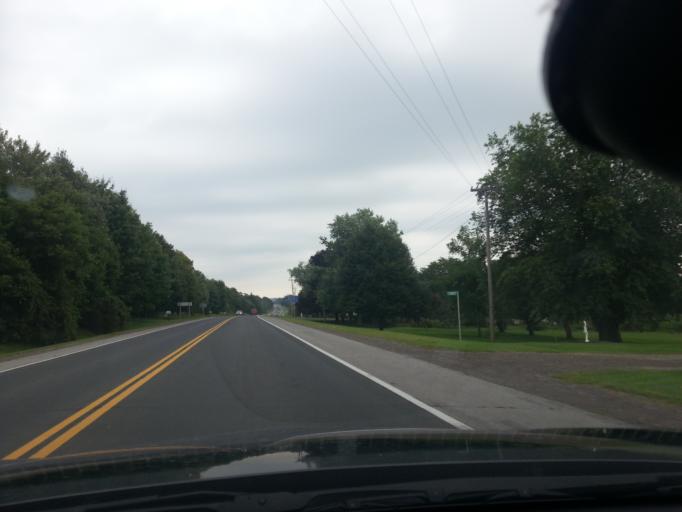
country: CA
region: Ontario
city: Prince Edward
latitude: 43.9891
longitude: -77.2037
